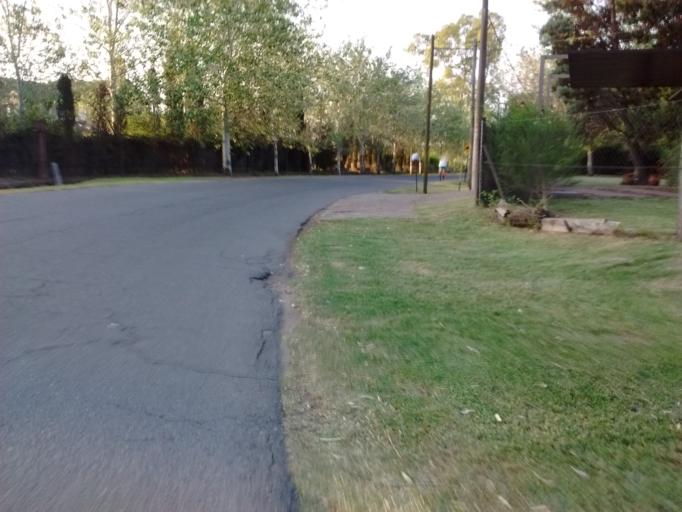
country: AR
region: Santa Fe
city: Funes
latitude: -32.9197
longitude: -60.7596
